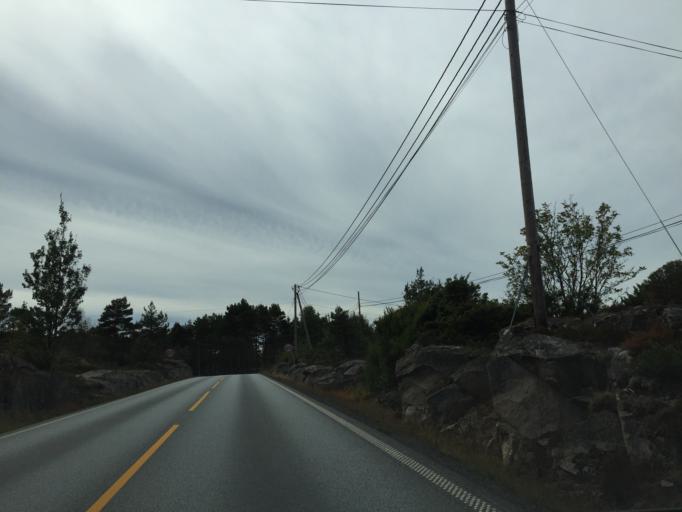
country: NO
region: Ostfold
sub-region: Hvaler
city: Skjaerhalden
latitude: 59.0716
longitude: 10.9348
